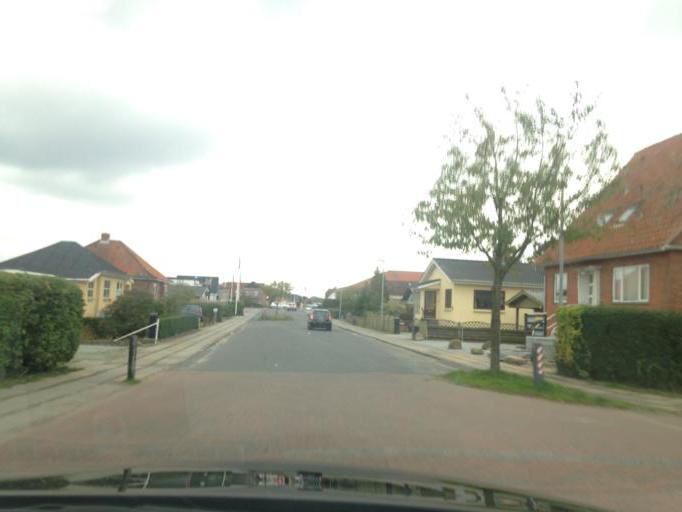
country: DK
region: South Denmark
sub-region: Kolding Kommune
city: Kolding
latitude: 55.4753
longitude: 9.4668
